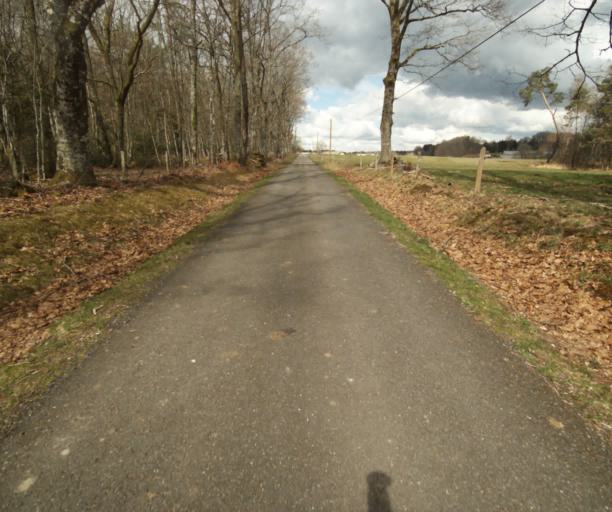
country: FR
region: Limousin
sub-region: Departement de la Correze
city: Correze
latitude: 45.2540
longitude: 1.9060
